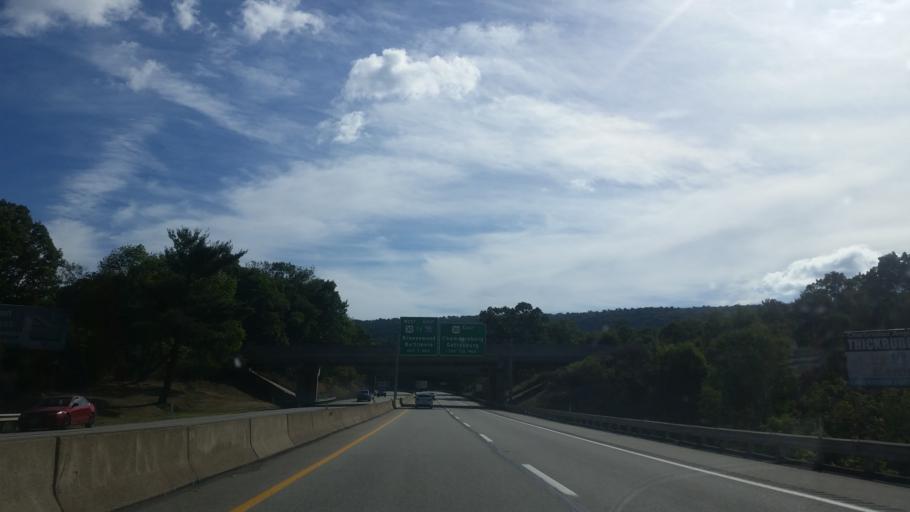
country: US
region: Pennsylvania
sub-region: Bedford County
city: Earlston
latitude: 39.9905
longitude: -78.2442
